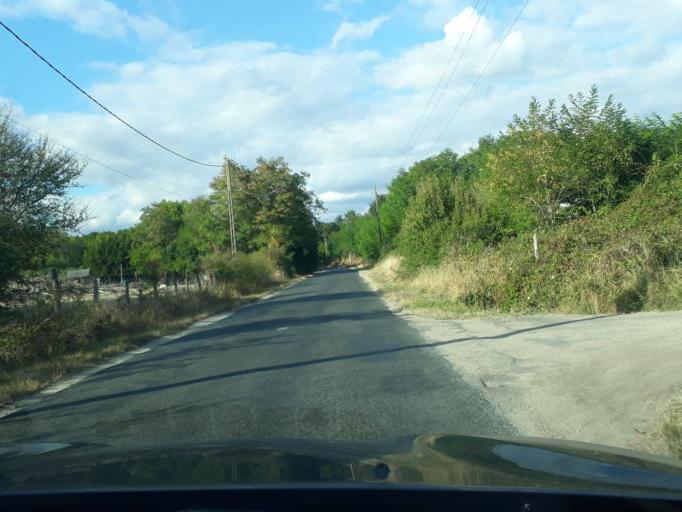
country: FR
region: Centre
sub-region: Departement du Loiret
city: Rebrechien
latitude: 47.9923
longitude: 2.0541
